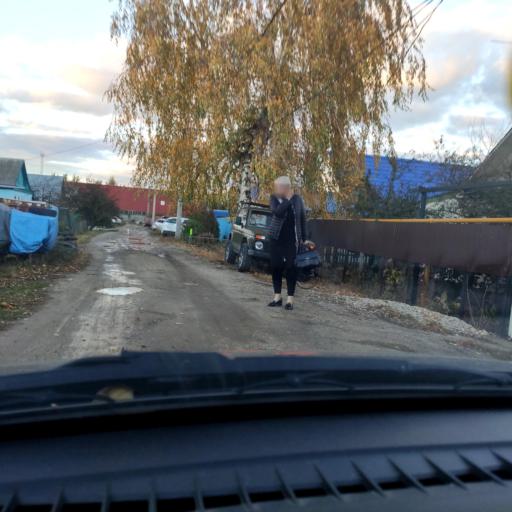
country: RU
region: Samara
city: Tol'yatti
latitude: 53.5395
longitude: 49.4218
